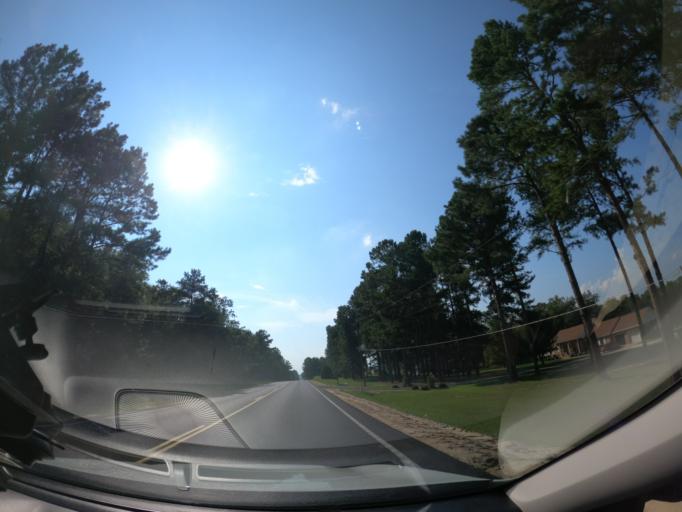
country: US
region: South Carolina
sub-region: Aiken County
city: Jackson
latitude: 33.4011
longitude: -81.7636
